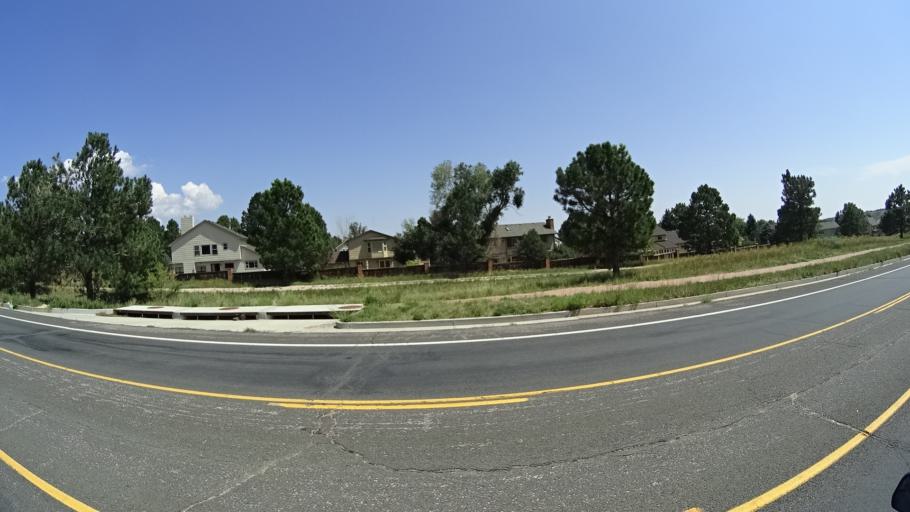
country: US
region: Colorado
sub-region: El Paso County
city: Manitou Springs
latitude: 38.9033
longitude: -104.8714
